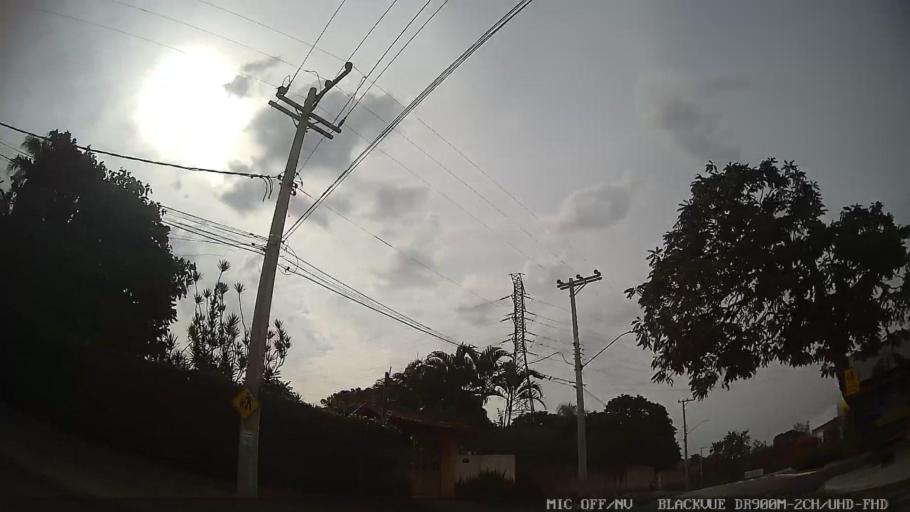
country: BR
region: Sao Paulo
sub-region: Indaiatuba
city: Indaiatuba
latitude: -23.0976
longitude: -47.1984
